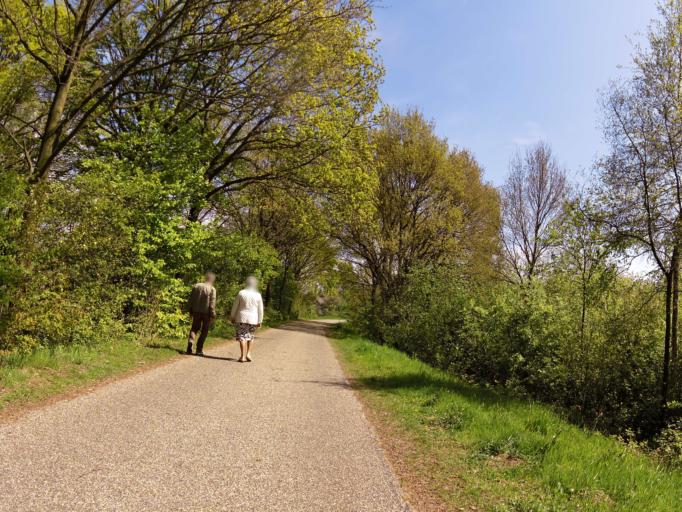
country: NL
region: North Brabant
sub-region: Gemeente Sint-Michielsgestel
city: Sint-Michielsgestel
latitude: 51.6728
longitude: 5.3970
